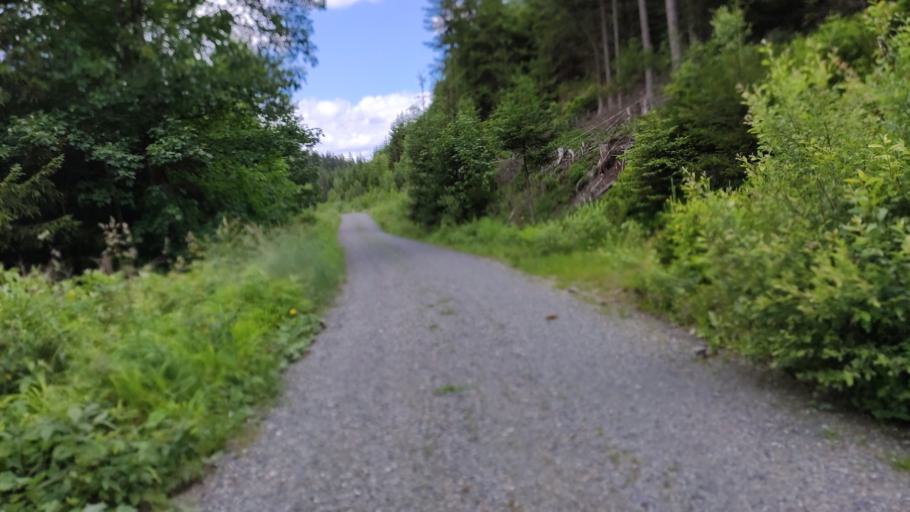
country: DE
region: Bavaria
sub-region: Upper Franconia
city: Tschirn
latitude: 50.3923
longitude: 11.4628
